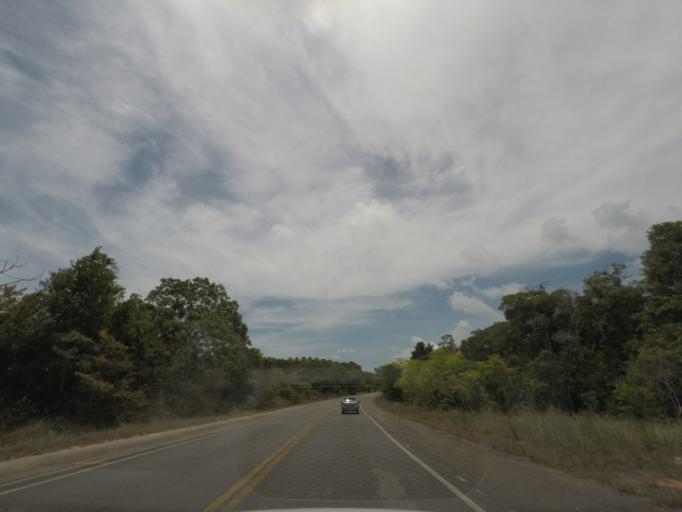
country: BR
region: Bahia
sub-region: Conde
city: Conde
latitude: -12.0297
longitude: -37.6980
